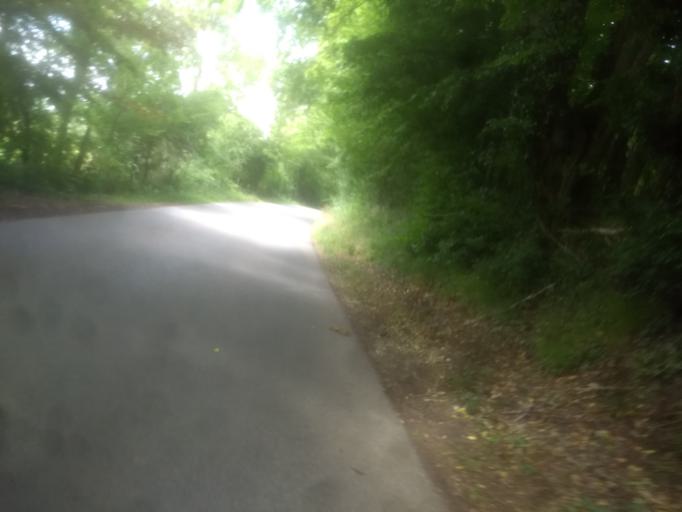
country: FR
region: Nord-Pas-de-Calais
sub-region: Departement du Pas-de-Calais
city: Mont-Saint-Eloi
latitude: 50.3409
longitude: 2.6884
